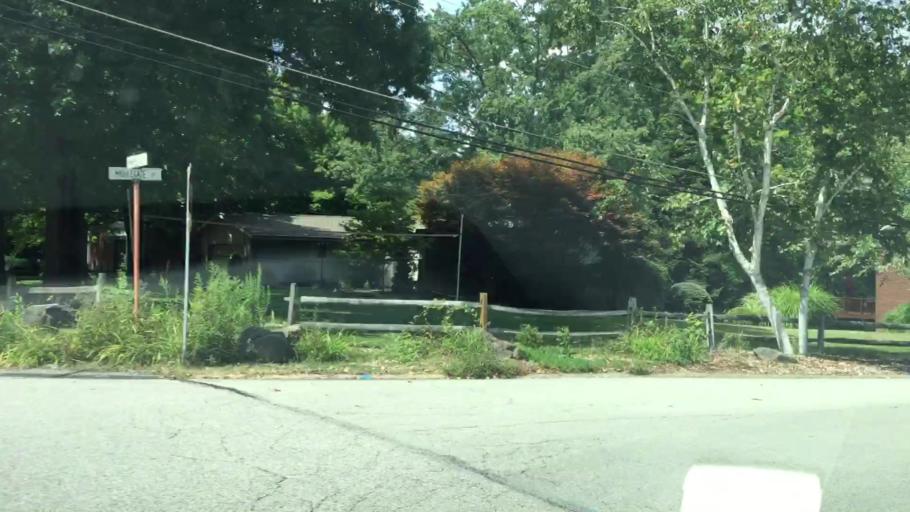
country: US
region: Pennsylvania
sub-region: Allegheny County
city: Bethel Park
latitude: 40.3145
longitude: -80.0624
